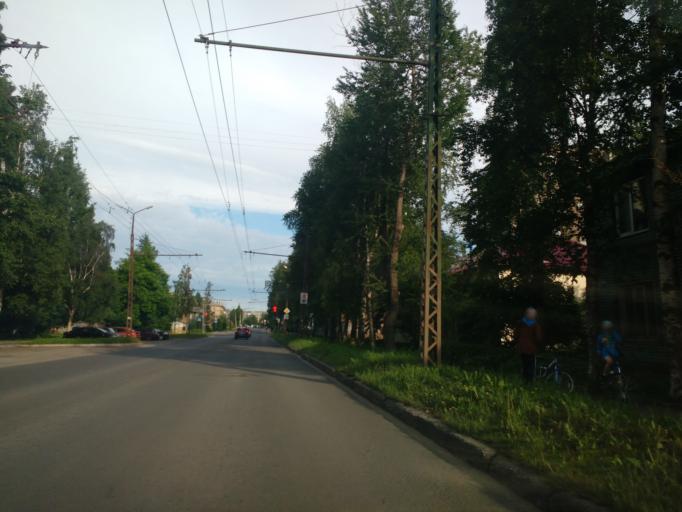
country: RU
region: Republic of Karelia
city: Petrozavodsk
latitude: 61.8097
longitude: 34.3252
